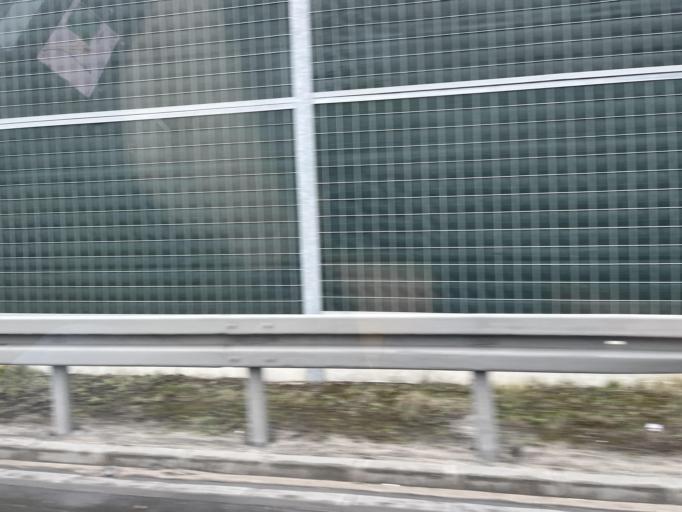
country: PL
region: Masovian Voivodeship
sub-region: Powiat zyrardowski
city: Wiskitki
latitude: 52.0865
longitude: 20.3606
